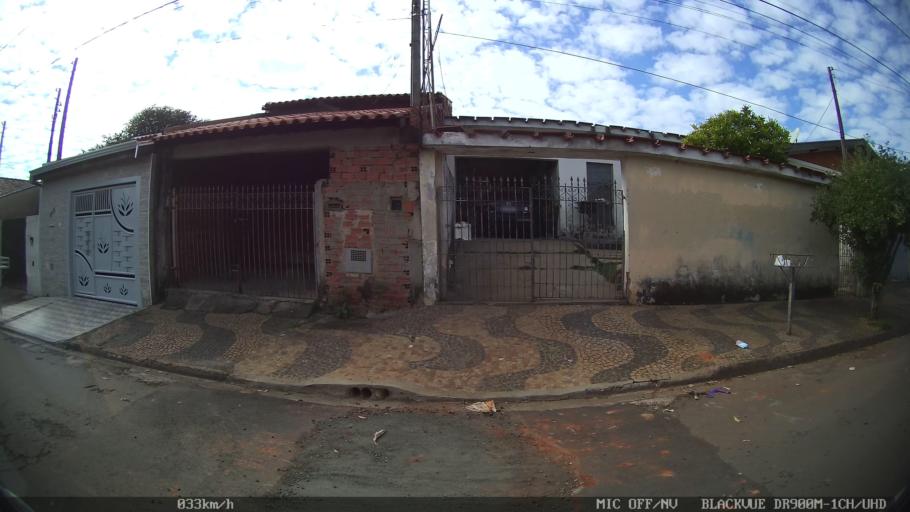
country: BR
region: Sao Paulo
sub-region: Santa Barbara D'Oeste
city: Santa Barbara d'Oeste
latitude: -22.7707
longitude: -47.3951
